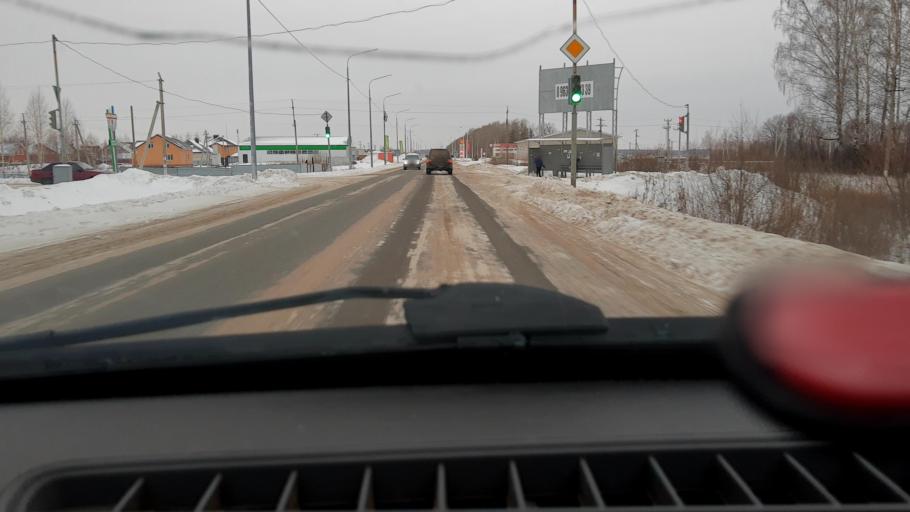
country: RU
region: Bashkortostan
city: Kabakovo
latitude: 54.6057
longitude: 56.1880
